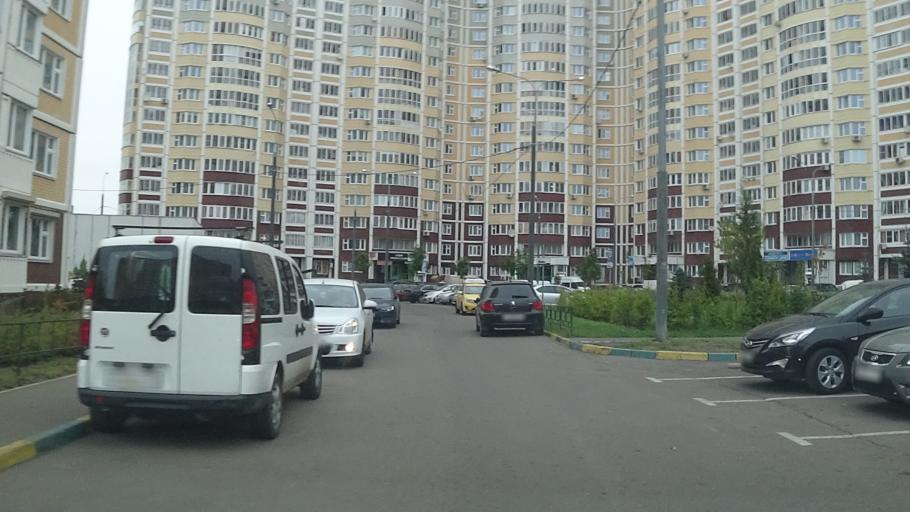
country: RU
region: Moskovskaya
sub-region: Leninskiy Rayon
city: Vnukovo
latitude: 55.6258
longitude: 37.3128
